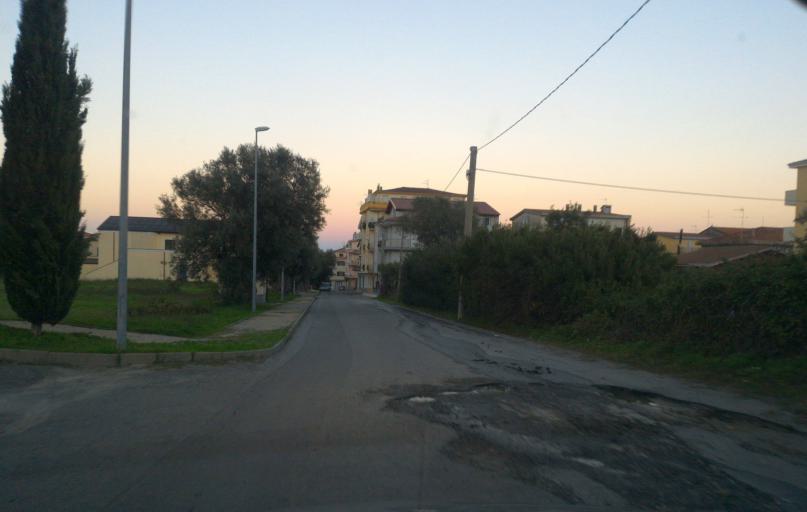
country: IT
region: Calabria
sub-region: Provincia di Crotone
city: Torretta
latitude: 39.4528
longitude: 17.0336
